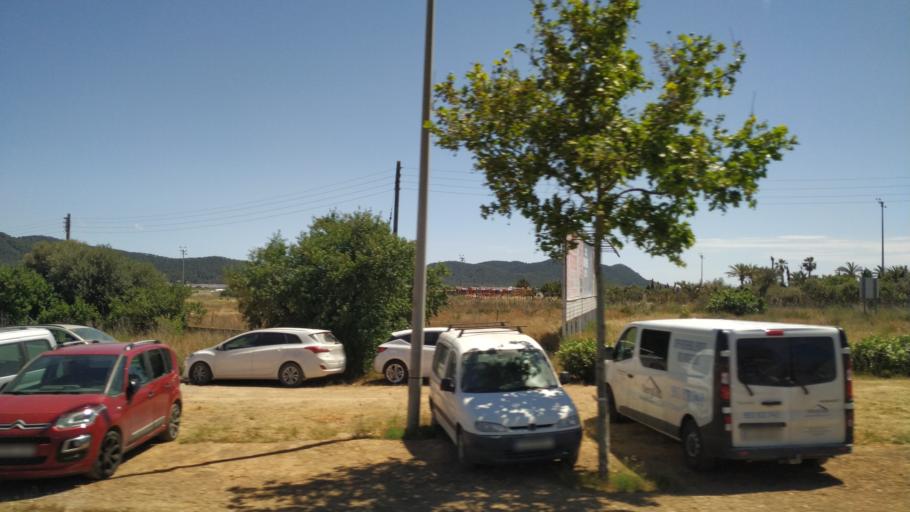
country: ES
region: Balearic Islands
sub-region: Illes Balears
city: Ibiza
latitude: 38.8822
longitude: 1.3783
